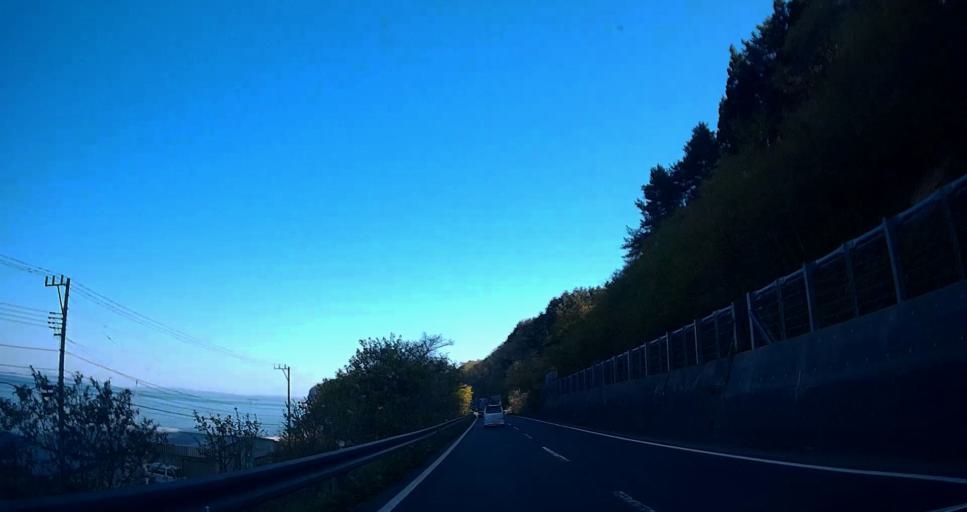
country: JP
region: Aomori
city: Mutsu
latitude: 41.4497
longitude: 141.1196
